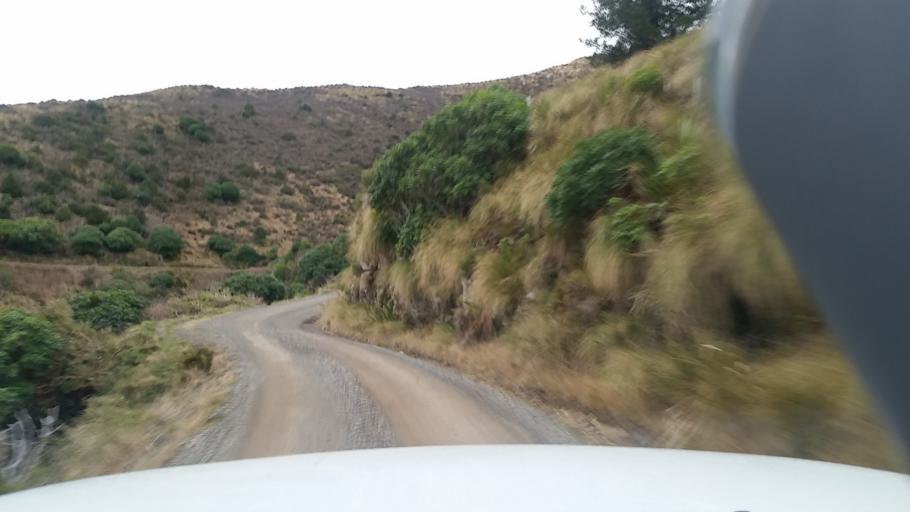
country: NZ
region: Canterbury
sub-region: Christchurch City
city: Christchurch
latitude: -43.8089
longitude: 172.8583
